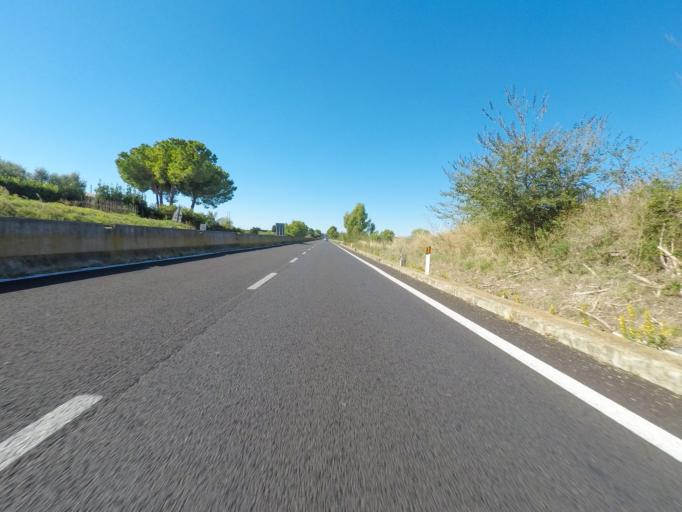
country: IT
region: Latium
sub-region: Provincia di Viterbo
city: Pescia Romana
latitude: 42.4032
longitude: 11.4967
